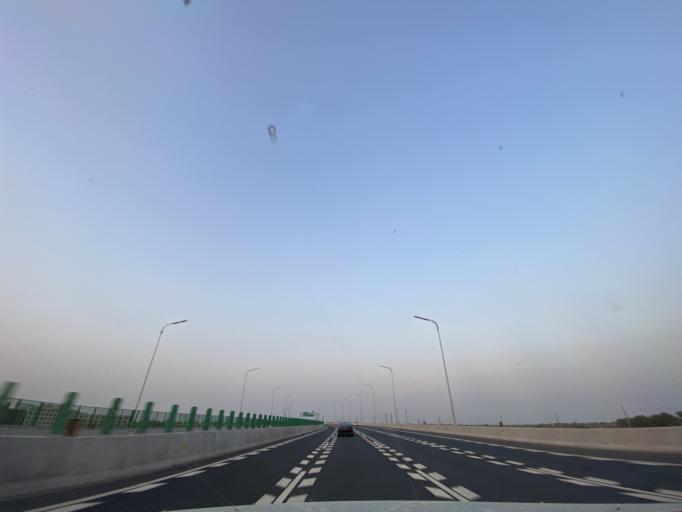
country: CN
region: Beijing
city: Xingfeng
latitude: 39.6938
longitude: 116.3734
